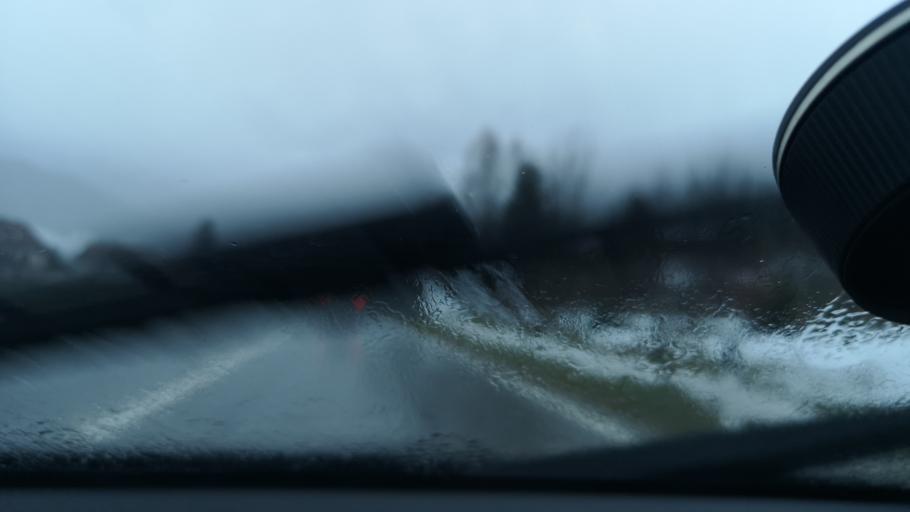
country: CH
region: Neuchatel
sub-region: Val-de-Travers District
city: Fleurier
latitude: 46.9163
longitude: 6.5977
